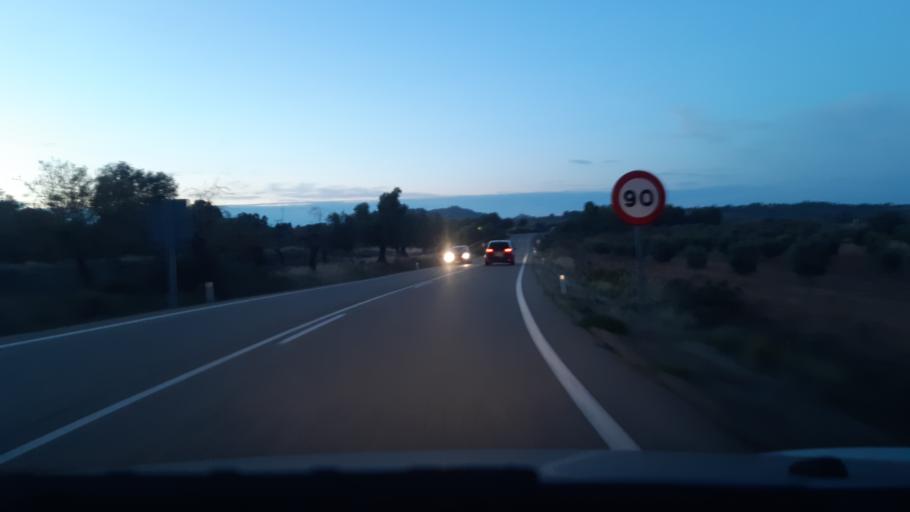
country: ES
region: Aragon
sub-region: Provincia de Teruel
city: Calaceite
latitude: 40.9837
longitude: 0.2004
